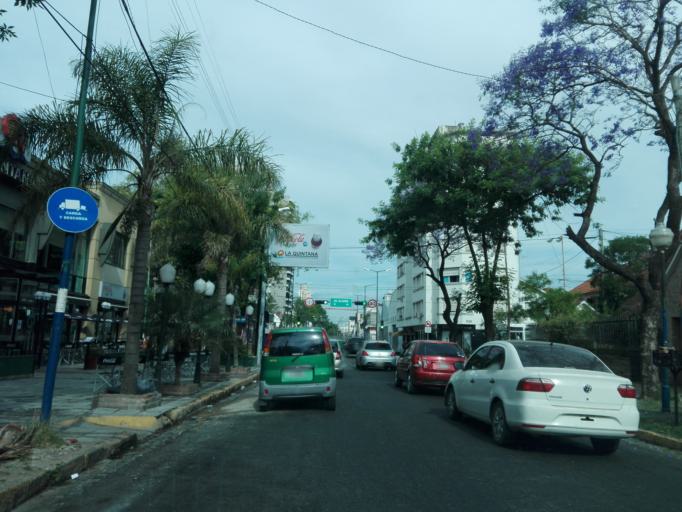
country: AR
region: Buenos Aires
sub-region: Partido de Lomas de Zamora
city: Lomas de Zamora
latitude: -34.7453
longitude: -58.3970
